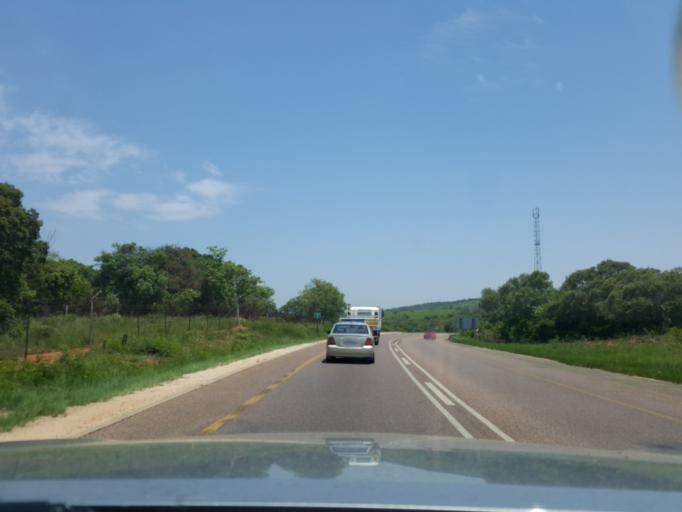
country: ZA
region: Limpopo
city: Thulamahashi
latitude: -24.8893
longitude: 31.1016
